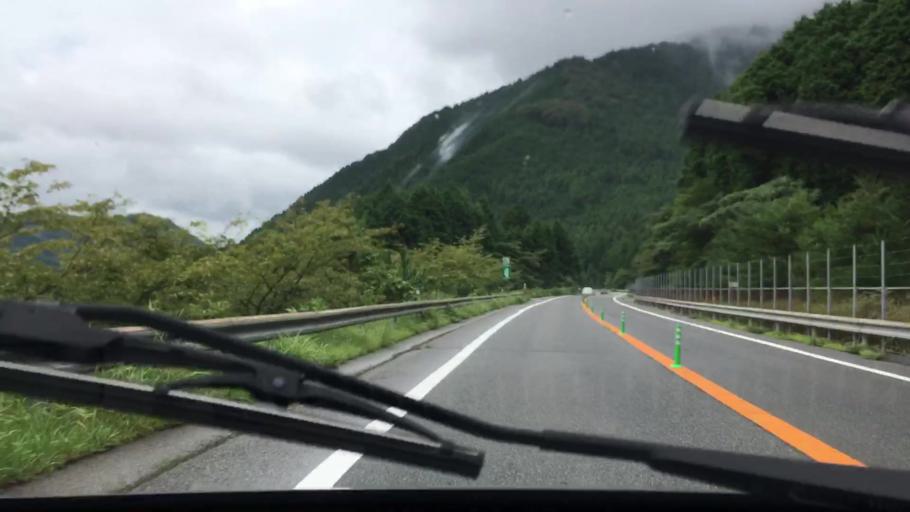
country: JP
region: Hyogo
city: Nishiwaki
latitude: 35.1360
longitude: 134.7895
